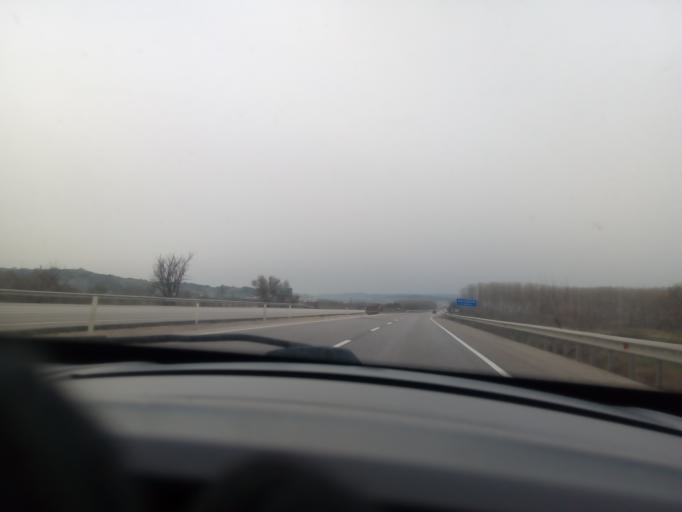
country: TR
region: Balikesir
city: Gobel
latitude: 39.9976
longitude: 28.2159
